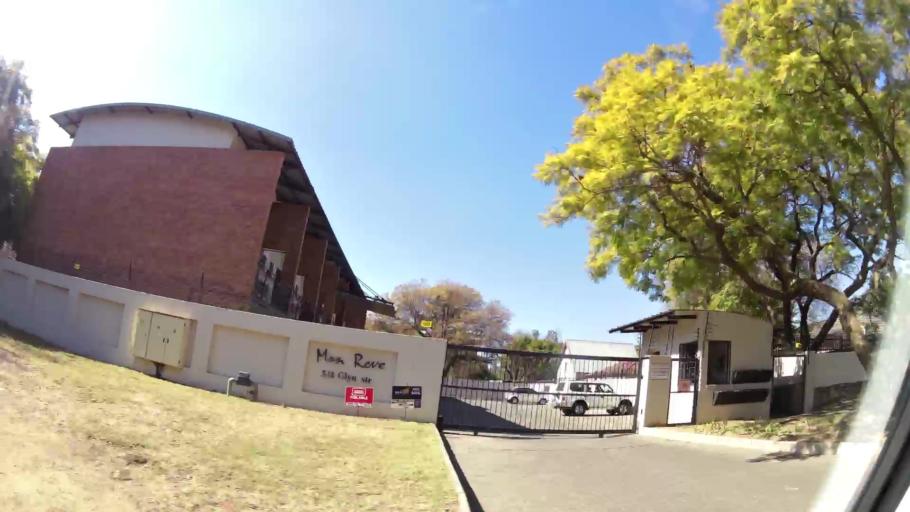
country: ZA
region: Gauteng
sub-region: City of Tshwane Metropolitan Municipality
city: Pretoria
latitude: -25.7526
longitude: 28.2427
